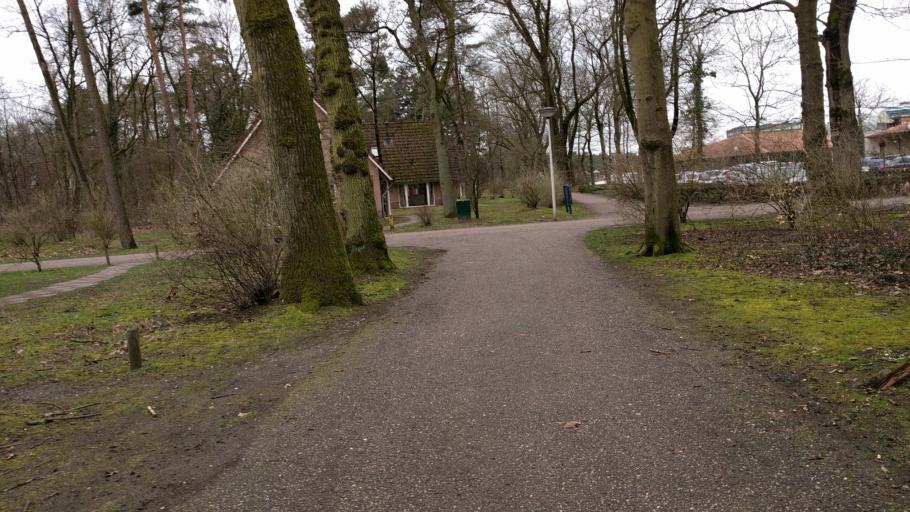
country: NL
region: Gelderland
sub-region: Gemeente Oldebroek
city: Oldebroek
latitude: 52.4391
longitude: 5.9554
